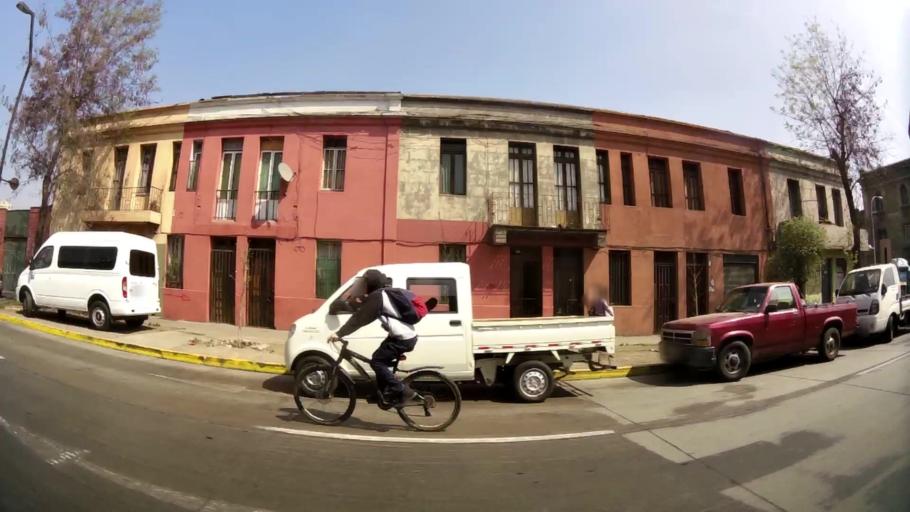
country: CL
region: Santiago Metropolitan
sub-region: Provincia de Santiago
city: Santiago
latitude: -33.4565
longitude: -70.6460
